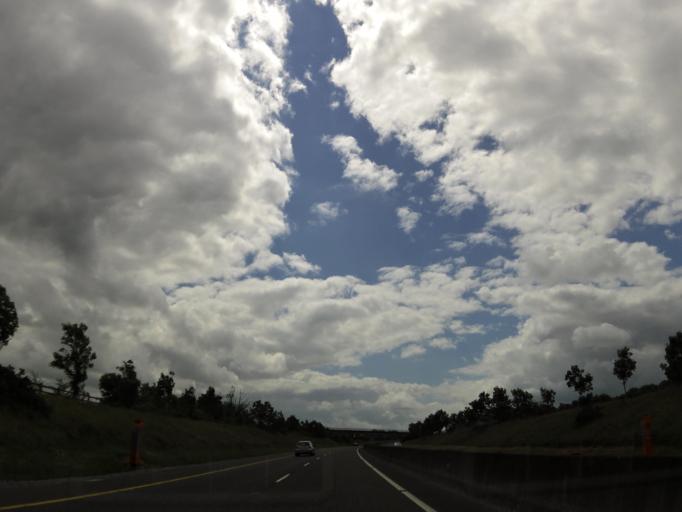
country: IE
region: Munster
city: Cashel
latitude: 52.5256
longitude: -7.8583
